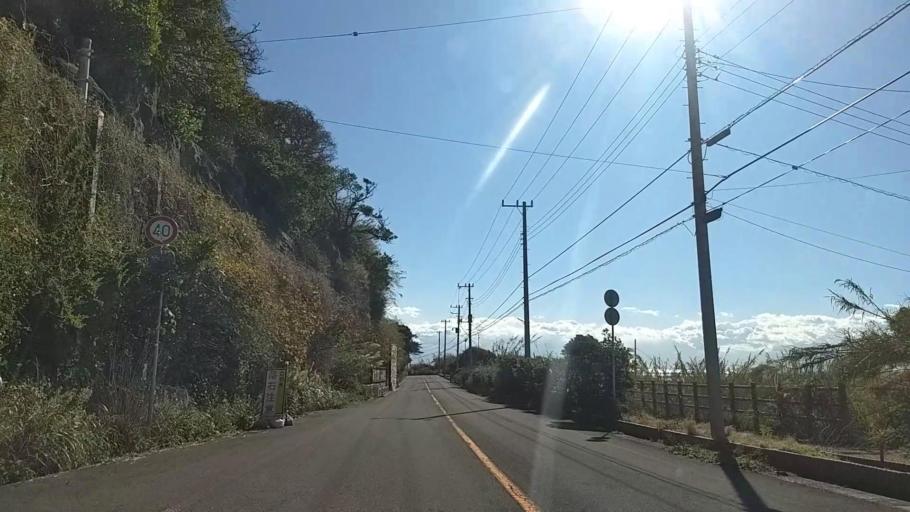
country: JP
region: Chiba
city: Tateyama
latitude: 34.9104
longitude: 139.8297
